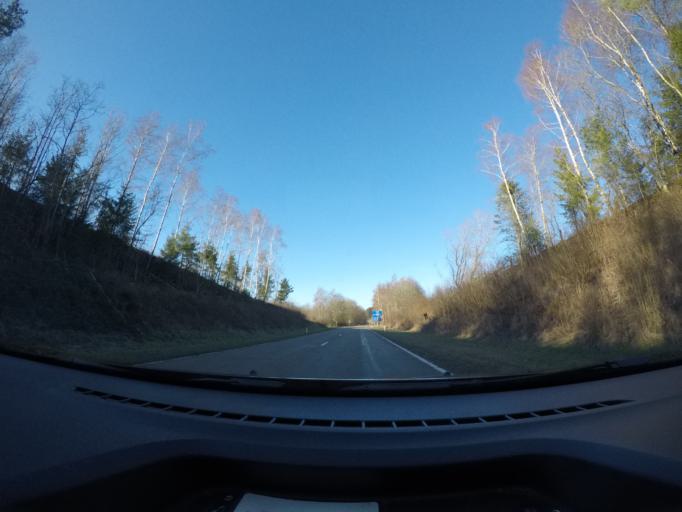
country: BE
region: Wallonia
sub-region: Province du Luxembourg
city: Bertrix
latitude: 49.8588
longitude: 5.2790
